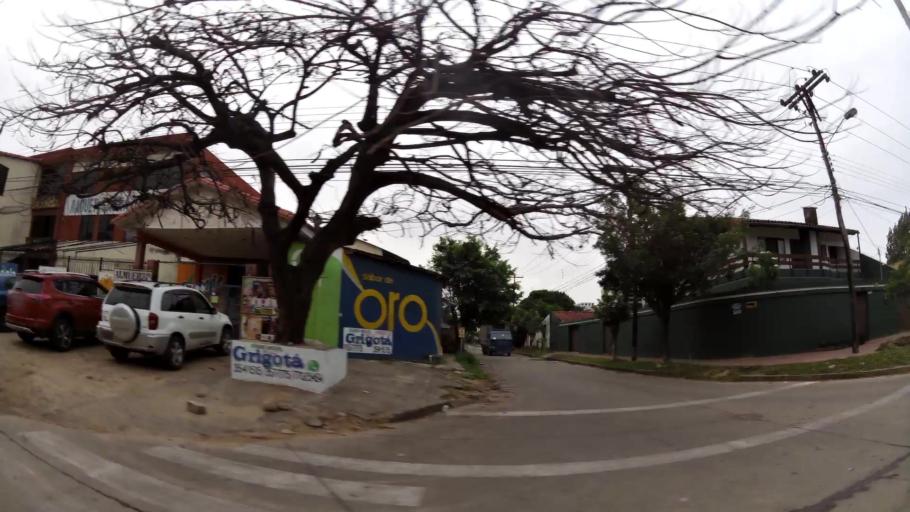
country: BO
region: Santa Cruz
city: Santa Cruz de la Sierra
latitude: -17.8111
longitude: -63.1786
